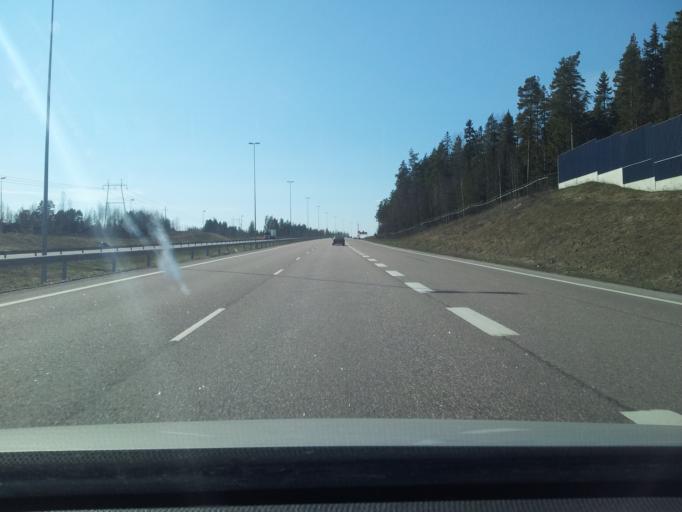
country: FI
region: Uusimaa
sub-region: Loviisa
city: Lovisa
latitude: 60.4605
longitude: 26.1910
